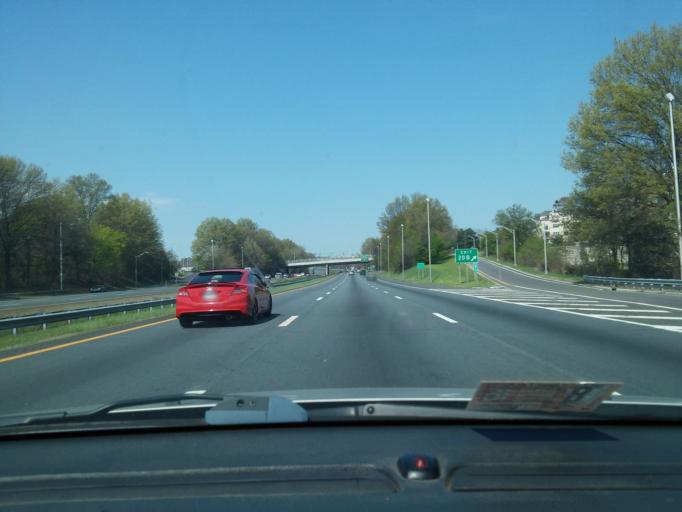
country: US
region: New Jersey
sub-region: Hunterdon County
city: Lebanon
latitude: 40.6472
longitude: -74.8299
